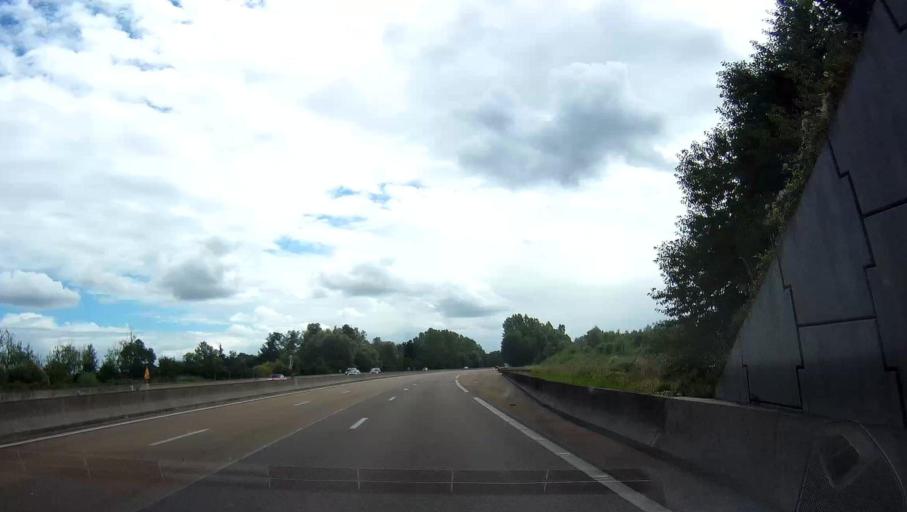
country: FR
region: Bourgogne
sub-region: Departement de la Cote-d'Or
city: Saint-Julien
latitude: 47.4029
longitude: 5.1828
